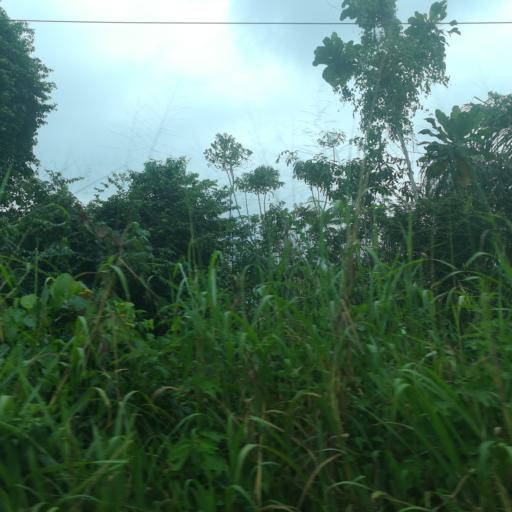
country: NG
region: Lagos
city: Ejirin
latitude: 6.6615
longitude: 3.8145
